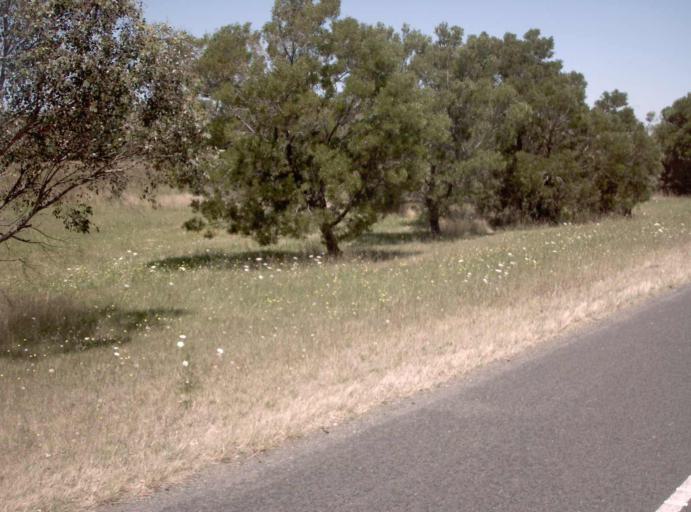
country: AU
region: Victoria
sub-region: Cardinia
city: Bunyip
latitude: -38.0754
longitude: 145.7169
